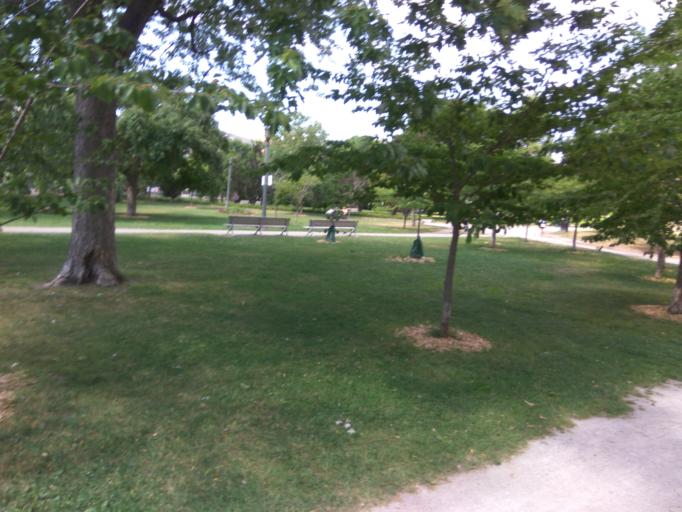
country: CA
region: Ontario
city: Toronto
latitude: 43.6461
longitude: -79.4128
